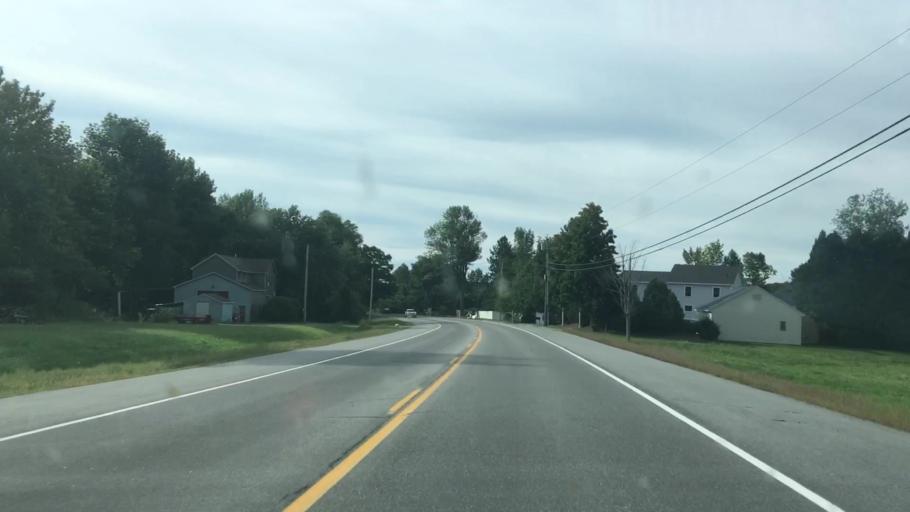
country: US
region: Maine
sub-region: Cumberland County
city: Cumberland Center
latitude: 43.7585
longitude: -70.3017
